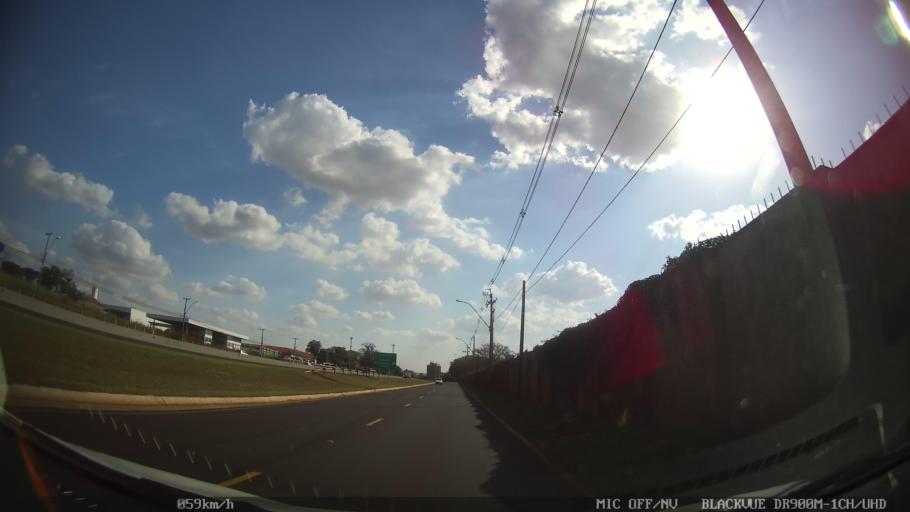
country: BR
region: Sao Paulo
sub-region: Ribeirao Preto
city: Ribeirao Preto
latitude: -21.1762
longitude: -47.8482
